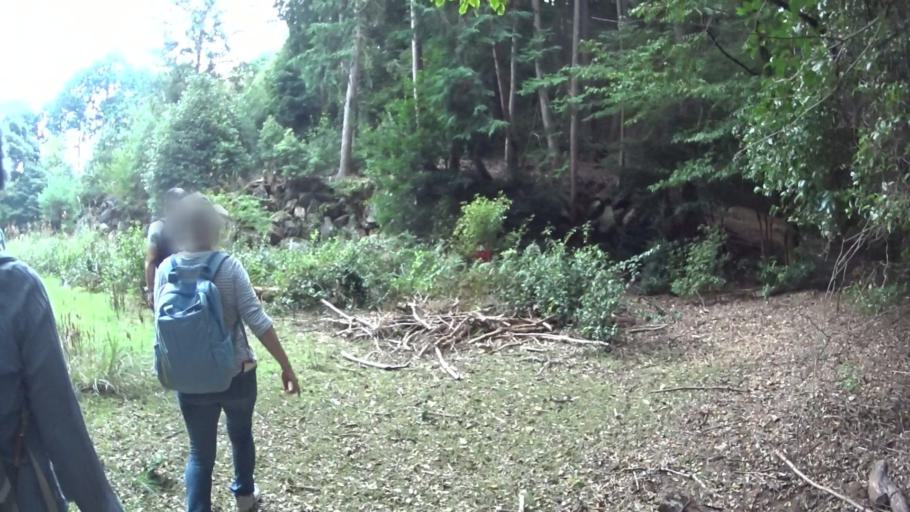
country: JP
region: Osaka
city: Kishiwada
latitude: 34.4987
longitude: 135.3313
